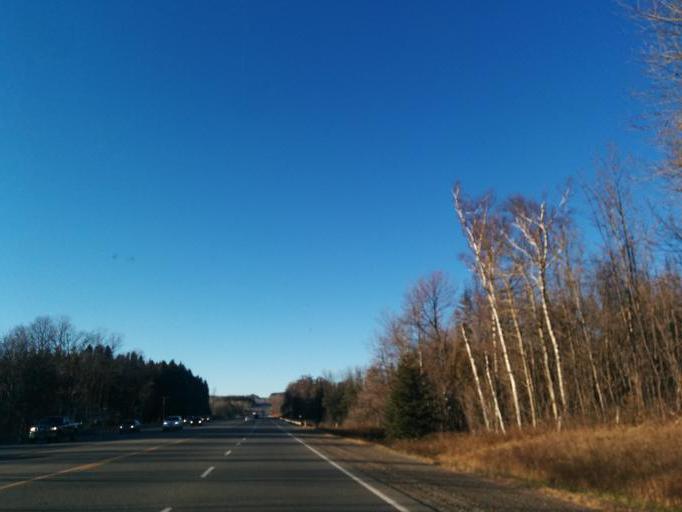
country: CA
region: Ontario
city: Orangeville
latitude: 43.8242
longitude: -79.9470
